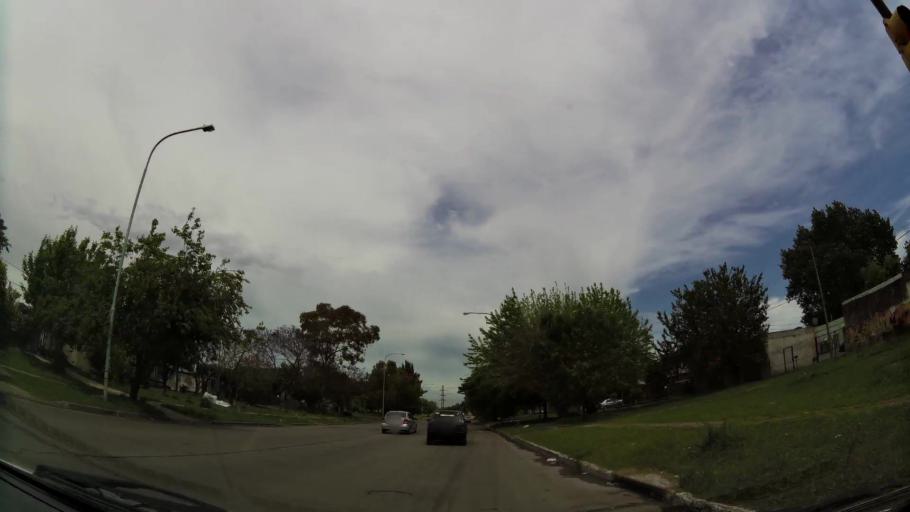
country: AR
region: Buenos Aires
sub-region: Partido de Quilmes
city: Quilmes
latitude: -34.7725
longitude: -58.2380
